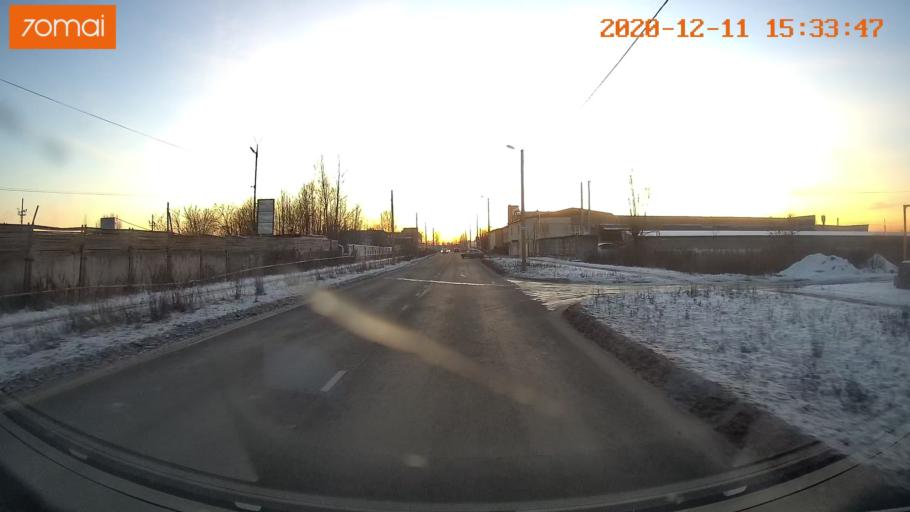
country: RU
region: Ivanovo
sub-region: Gorod Ivanovo
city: Ivanovo
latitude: 57.0493
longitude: 40.9442
